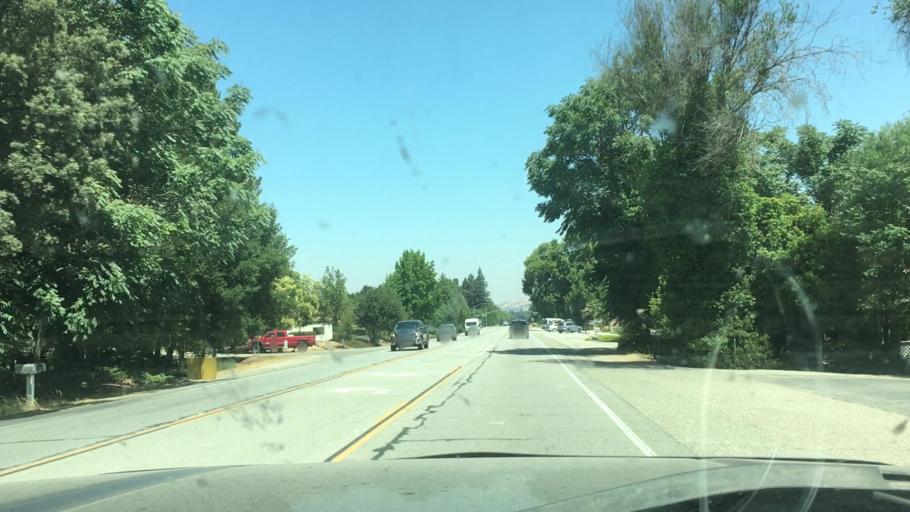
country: US
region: California
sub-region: San Luis Obispo County
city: Atascadero
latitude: 35.4708
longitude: -120.6693
